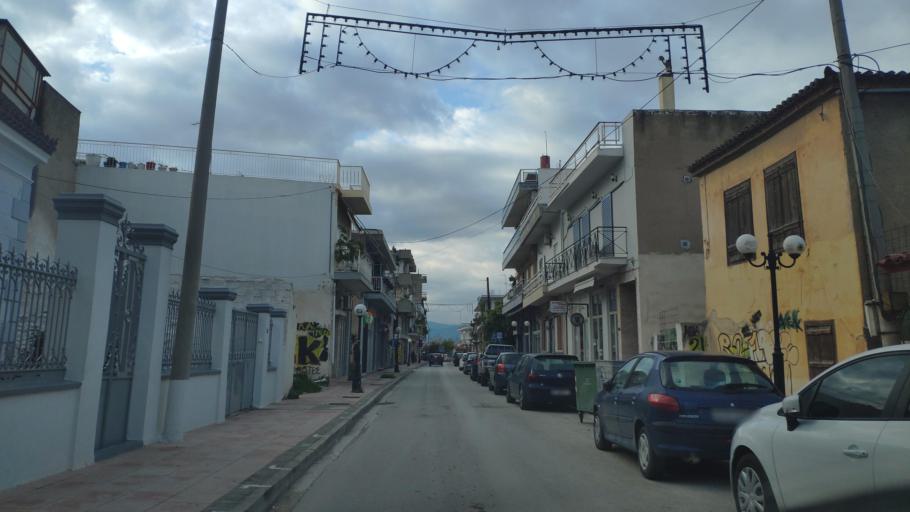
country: GR
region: Peloponnese
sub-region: Nomos Argolidos
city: Argos
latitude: 37.6323
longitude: 22.7245
